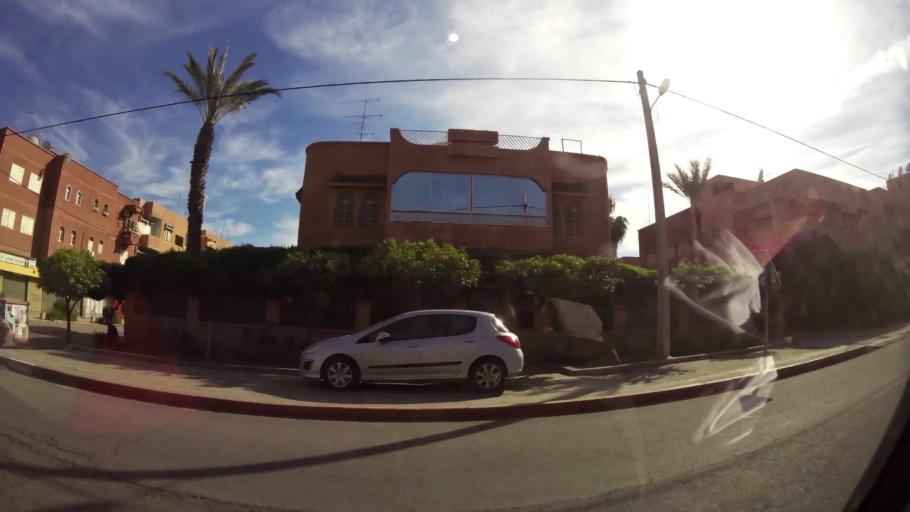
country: MA
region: Marrakech-Tensift-Al Haouz
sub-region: Marrakech
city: Marrakesh
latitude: 31.6555
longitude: -8.0115
